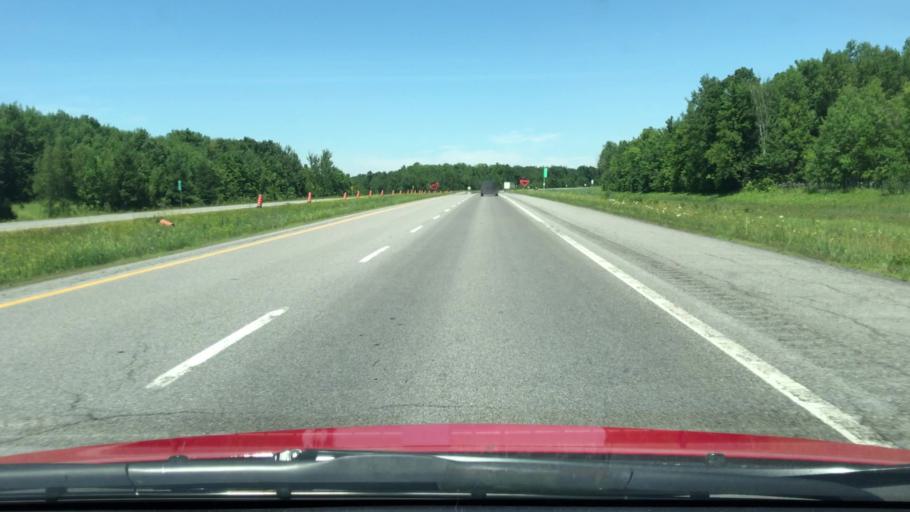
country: CA
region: Quebec
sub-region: Monteregie
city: Napierville
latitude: 45.1603
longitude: -73.4676
